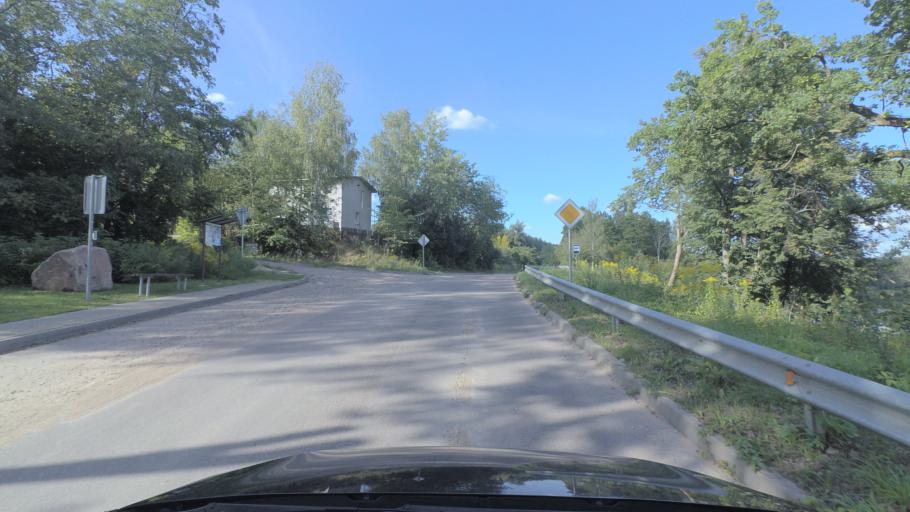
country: LT
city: Nemencine
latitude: 54.8498
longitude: 25.3737
